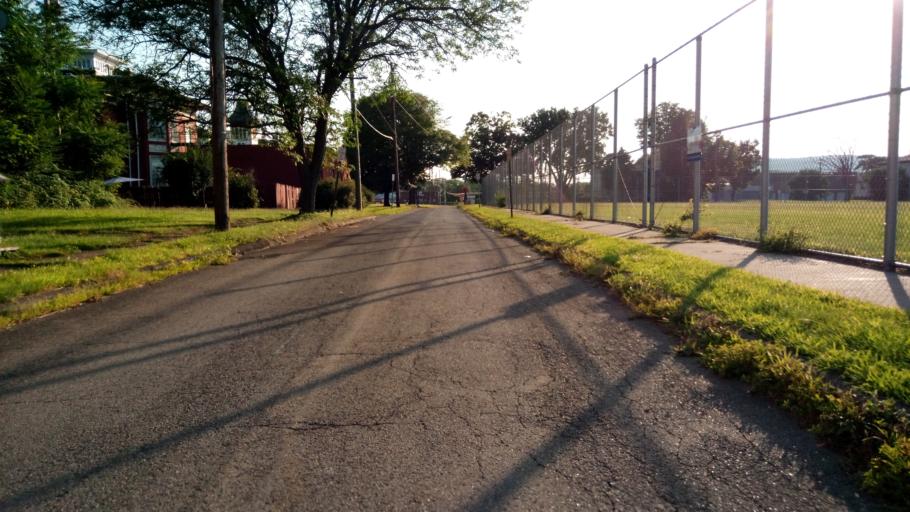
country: US
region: New York
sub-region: Chemung County
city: Elmira
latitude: 42.0944
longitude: -76.8026
